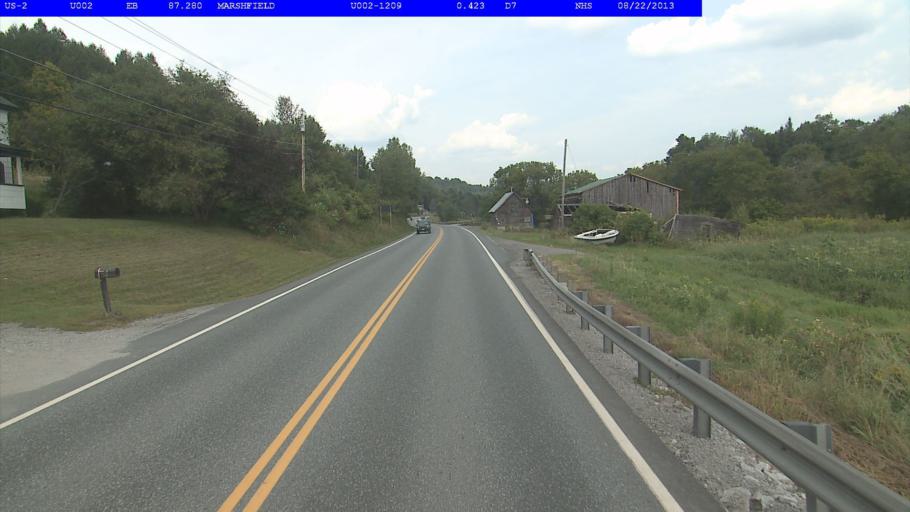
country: US
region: Vermont
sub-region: Washington County
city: Barre
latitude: 44.2837
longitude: -72.4158
